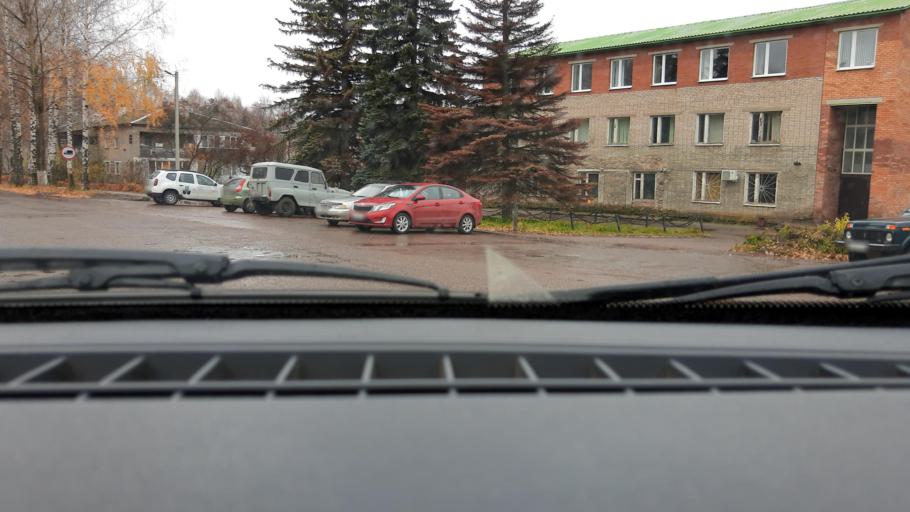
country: RU
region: Bashkortostan
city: Avdon
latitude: 54.8204
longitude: 55.7011
